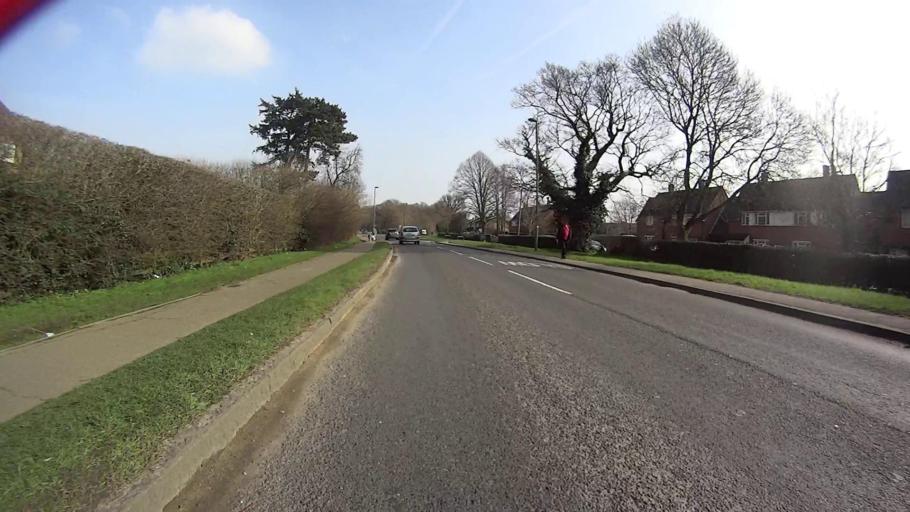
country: GB
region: England
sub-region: Surrey
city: Reigate
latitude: 51.2238
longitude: -0.1969
